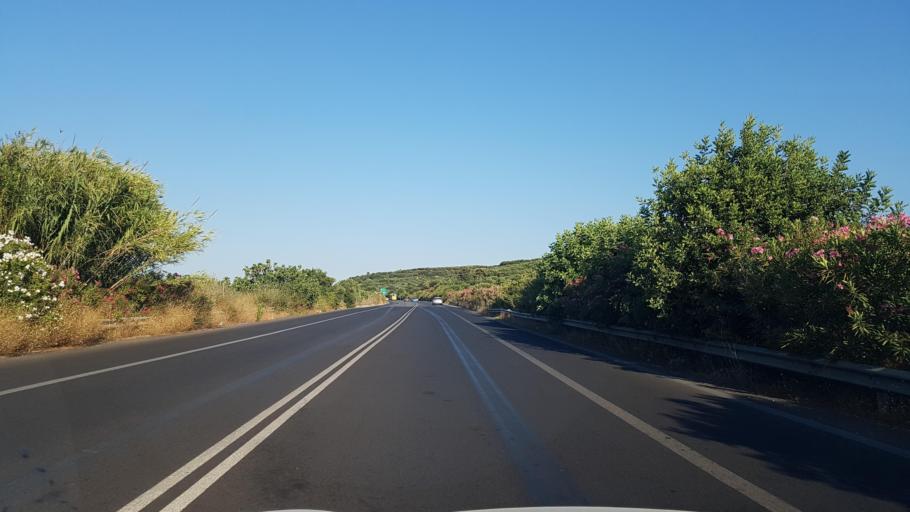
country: GR
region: Crete
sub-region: Nomos Chanias
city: Kolympari
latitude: 35.5258
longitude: 23.8006
